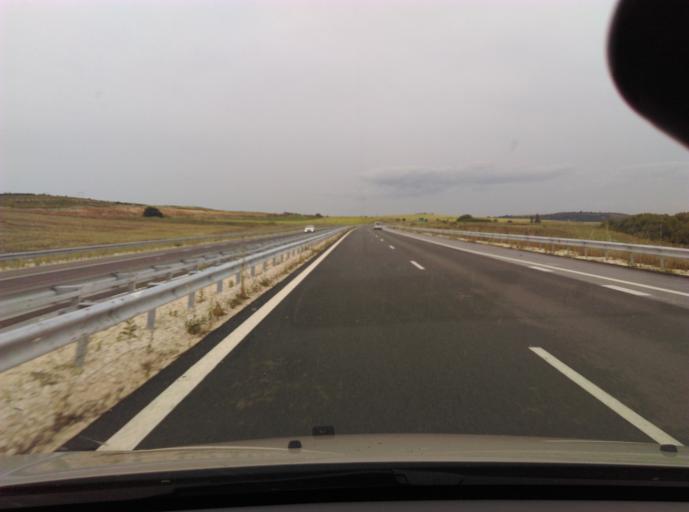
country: BG
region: Stara Zagora
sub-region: Obshtina Chirpan
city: Chirpan
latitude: 42.1185
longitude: 25.3930
